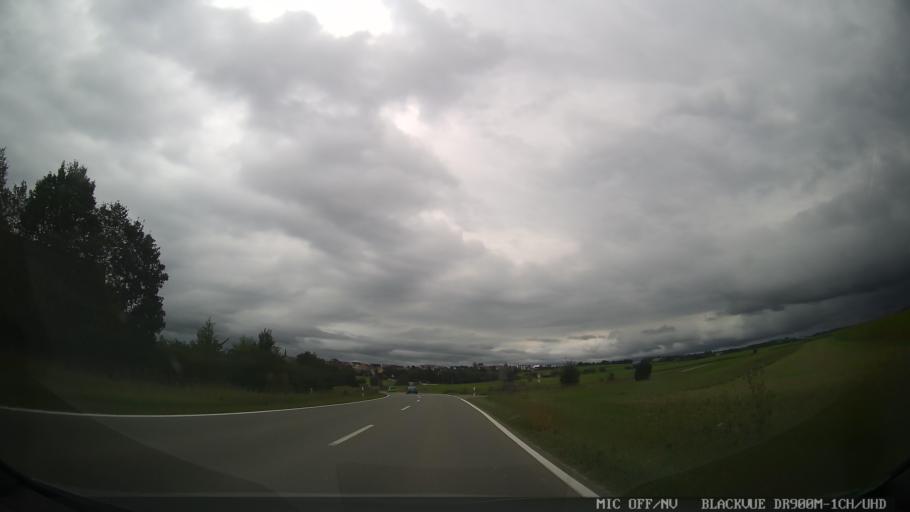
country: DE
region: Baden-Wuerttemberg
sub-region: Freiburg Region
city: Neuhausen ob Eck
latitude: 47.9806
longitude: 8.9277
